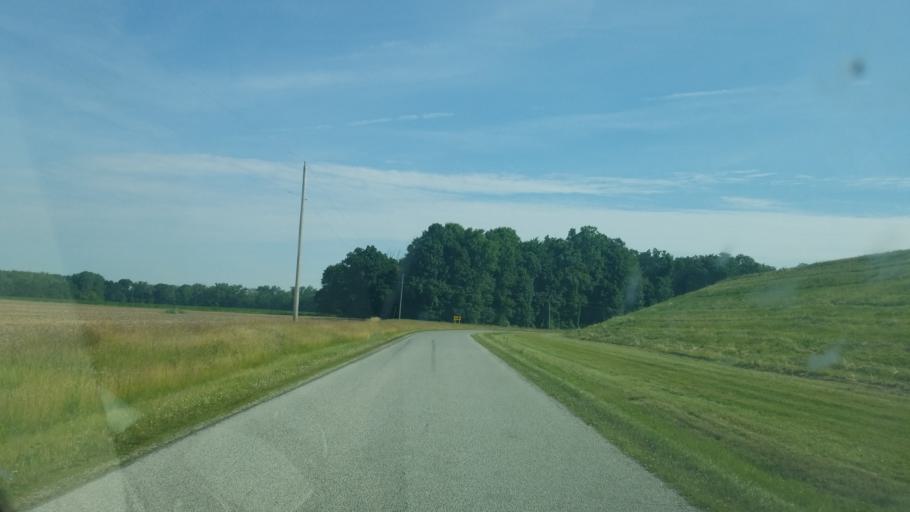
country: US
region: Ohio
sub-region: Hancock County
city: Findlay
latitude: 41.0269
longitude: -83.5807
